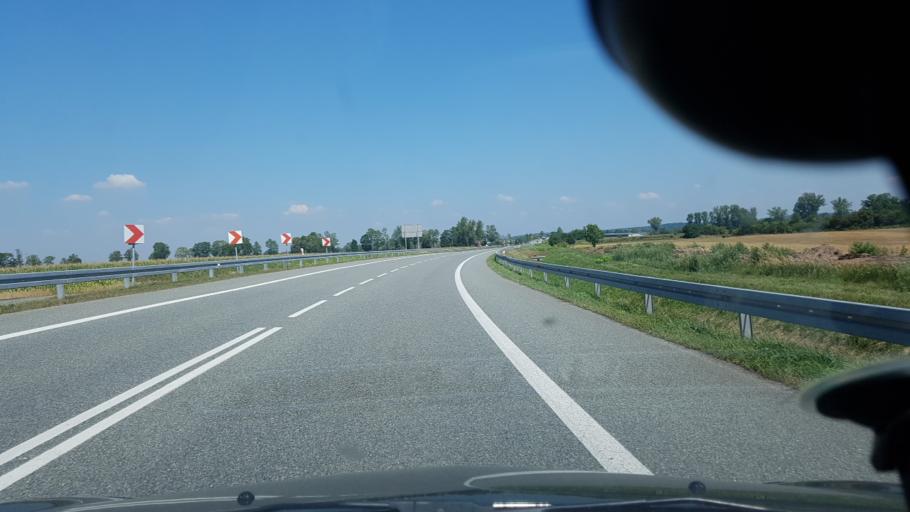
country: PL
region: Silesian Voivodeship
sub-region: Powiat wodzislawski
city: Olza
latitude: 49.9444
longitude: 18.3267
